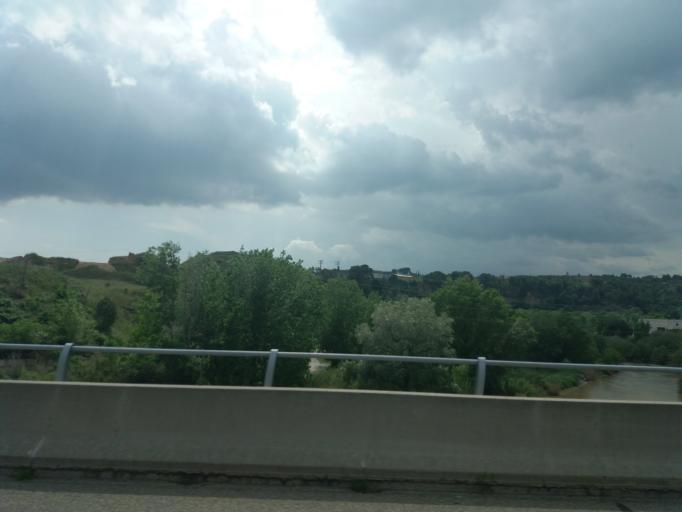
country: ES
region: Catalonia
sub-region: Provincia de Barcelona
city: Olesa de Montserrat
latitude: 41.5347
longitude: 1.8992
